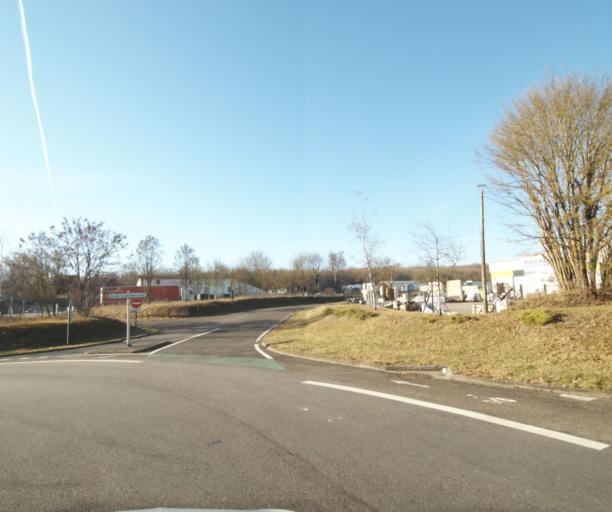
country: FR
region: Lorraine
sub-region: Departement de Meurthe-et-Moselle
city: Laxou
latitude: 48.6951
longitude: 6.1036
